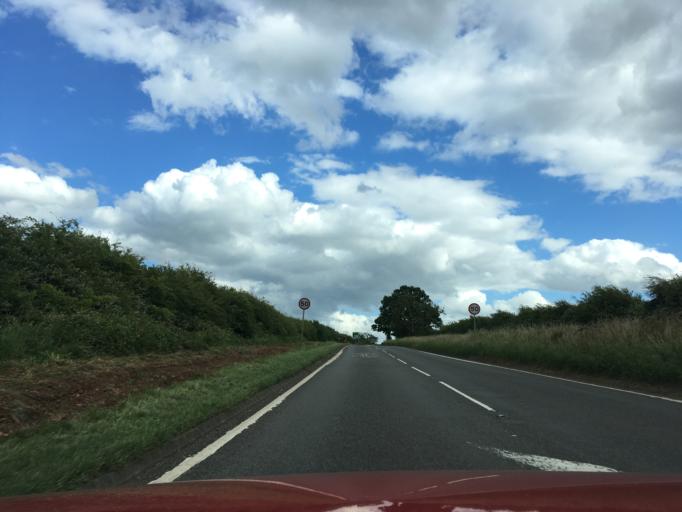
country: GB
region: England
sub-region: Leicestershire
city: Market Bosworth
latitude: 52.6193
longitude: -1.4777
